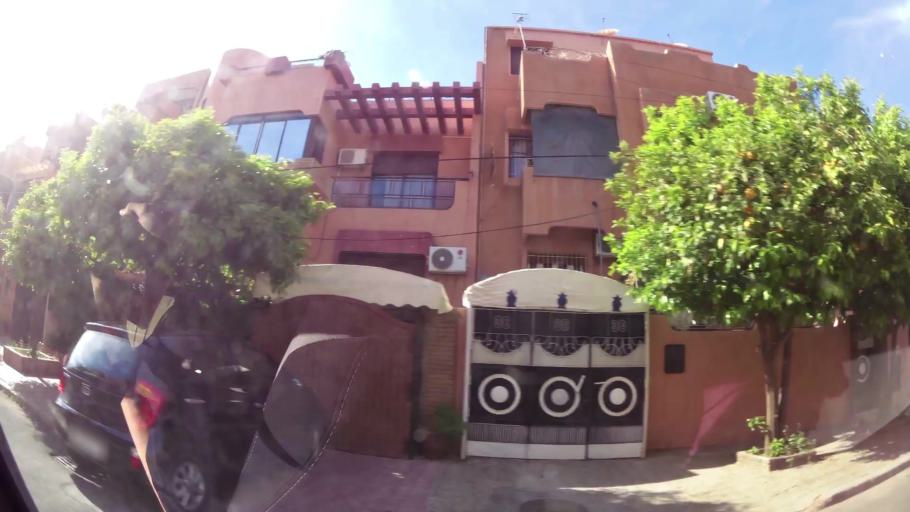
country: MA
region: Marrakech-Tensift-Al Haouz
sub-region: Marrakech
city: Marrakesh
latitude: 31.6533
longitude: -8.0064
